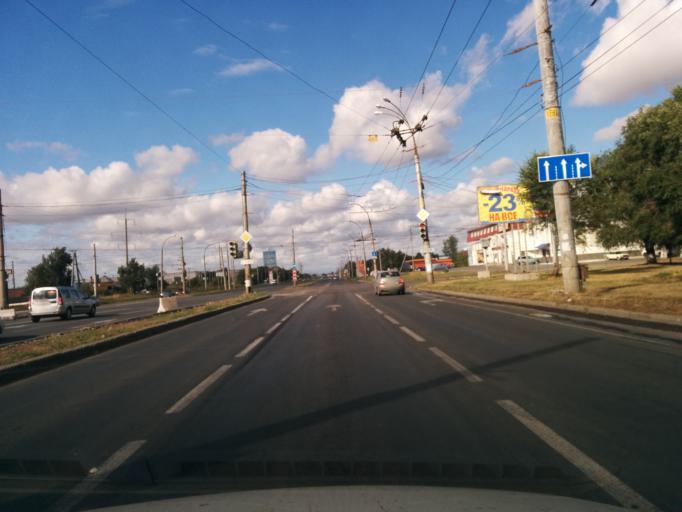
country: RU
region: Samara
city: Tol'yatti
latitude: 53.5386
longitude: 49.2637
